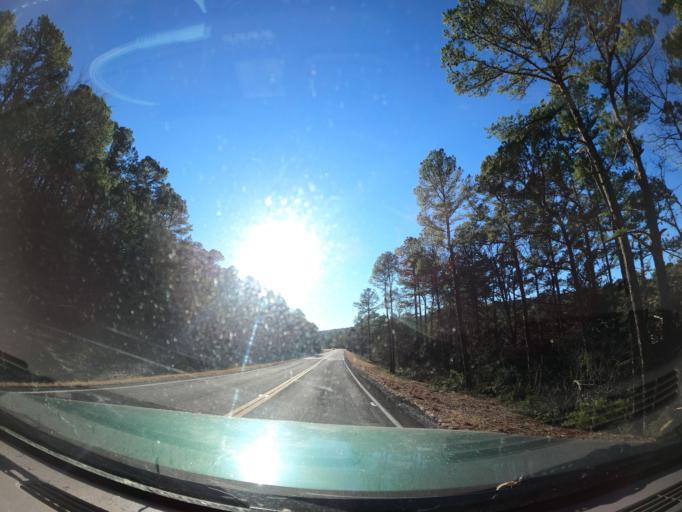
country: US
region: Oklahoma
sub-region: Latimer County
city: Wilburton
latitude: 34.9842
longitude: -95.3553
